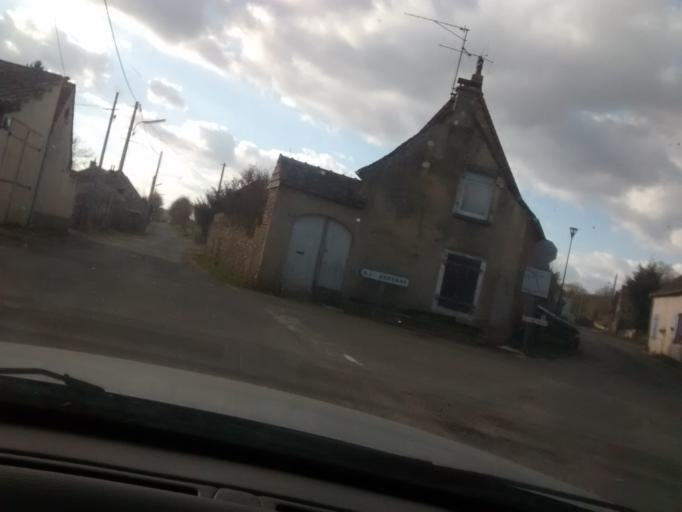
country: FR
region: Pays de la Loire
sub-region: Departement de la Sarthe
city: Le Breil-sur-Merize
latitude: 47.9749
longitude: 0.4599
